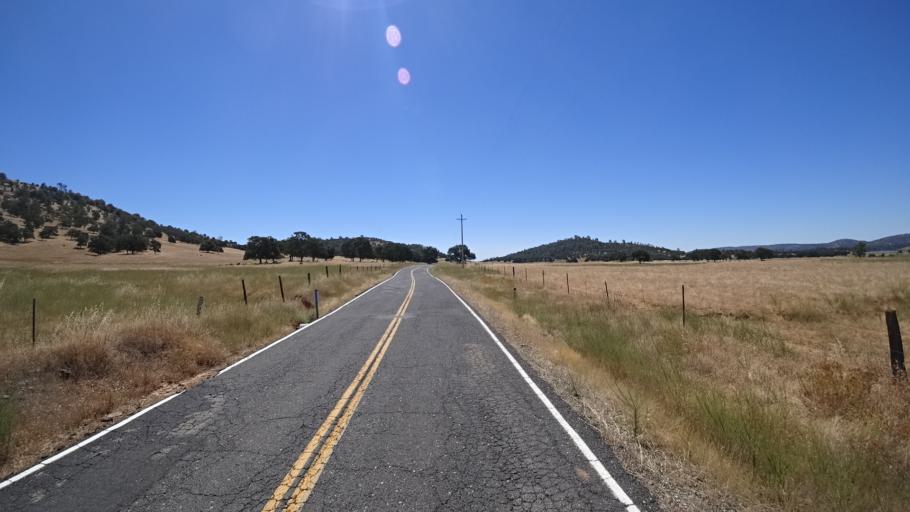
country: US
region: California
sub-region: Calaveras County
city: Copperopolis
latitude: 38.0152
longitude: -120.6754
